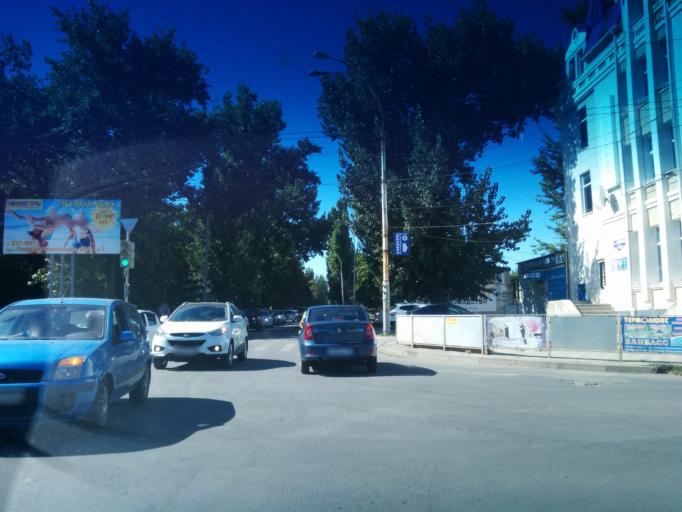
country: RU
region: Rostov
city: Shakhty
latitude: 47.7101
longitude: 40.2179
